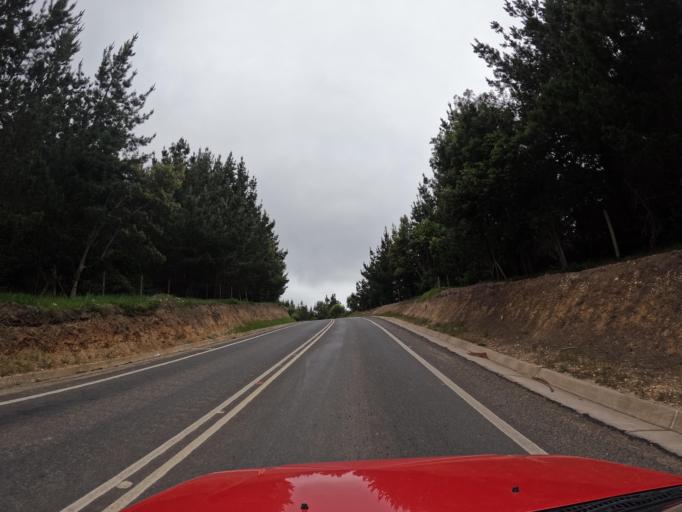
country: CL
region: O'Higgins
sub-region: Provincia de Colchagua
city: Santa Cruz
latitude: -34.5476
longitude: -72.0214
